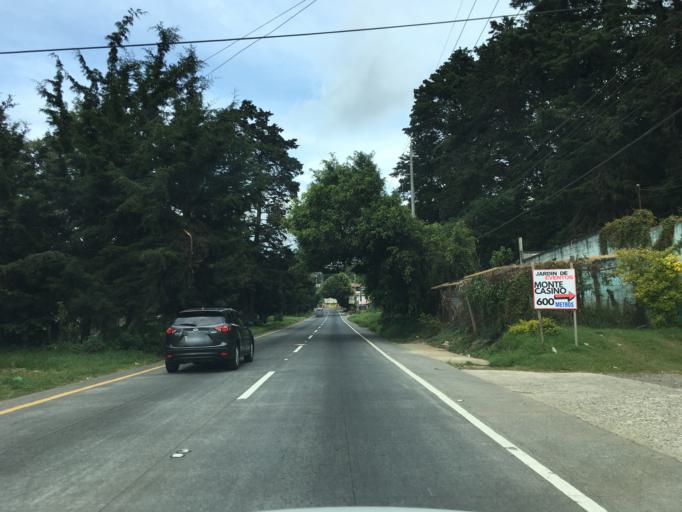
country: GT
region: Sacatepequez
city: Santa Lucia Milpas Altas
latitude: 14.5765
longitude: -90.6672
